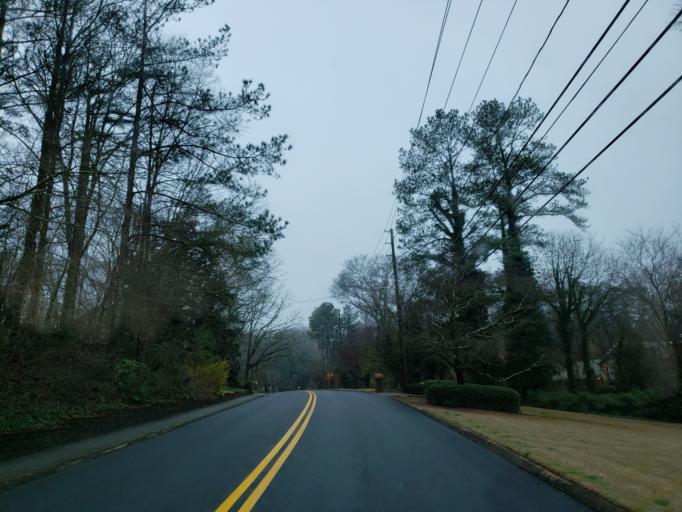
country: US
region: Georgia
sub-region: Cobb County
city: Marietta
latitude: 33.9340
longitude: -84.5677
